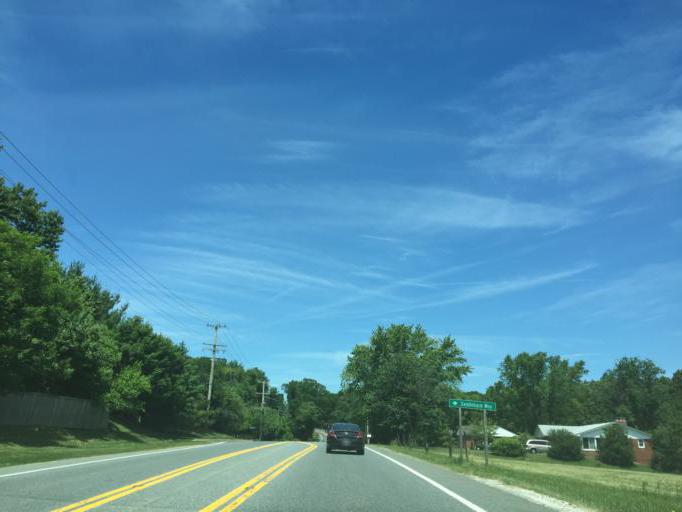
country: US
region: Maryland
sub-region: Harford County
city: North Bel Air
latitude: 39.5709
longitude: -76.3341
